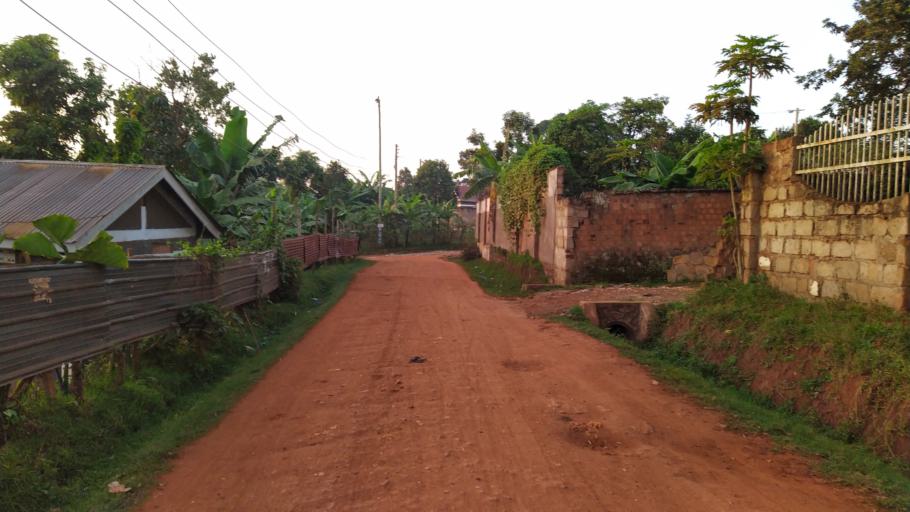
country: UG
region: Central Region
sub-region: Kampala District
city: Kampala
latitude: 0.2717
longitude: 32.5750
